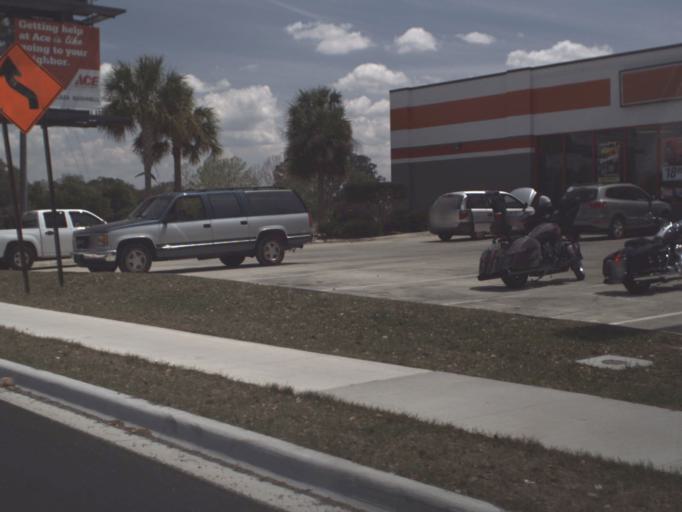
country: US
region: Florida
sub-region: Sumter County
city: Bushnell
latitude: 28.6686
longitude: -82.1366
